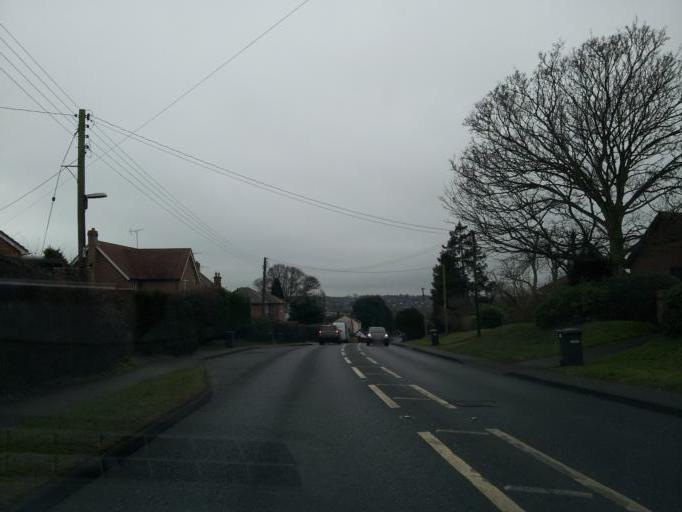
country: GB
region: England
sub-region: Essex
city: Manningtree
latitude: 51.9626
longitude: 1.0626
